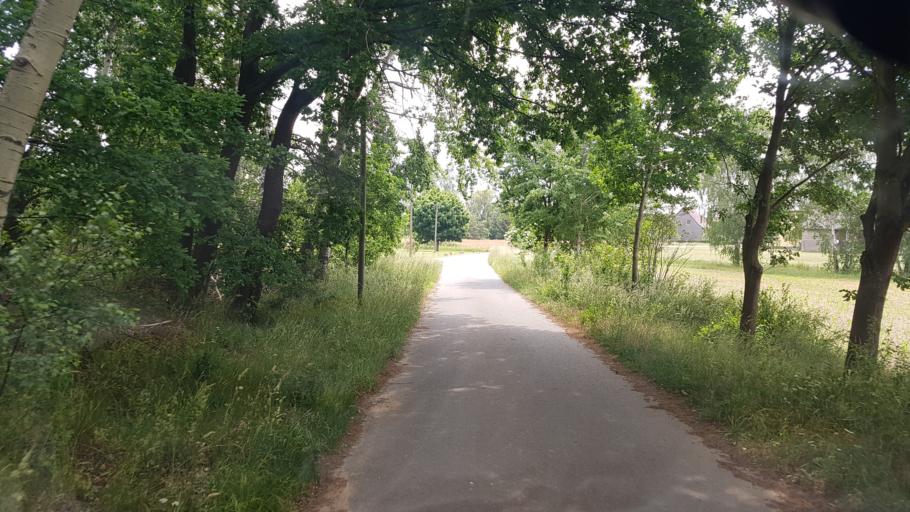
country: DE
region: Brandenburg
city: Lebusa
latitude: 51.8156
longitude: 13.4418
